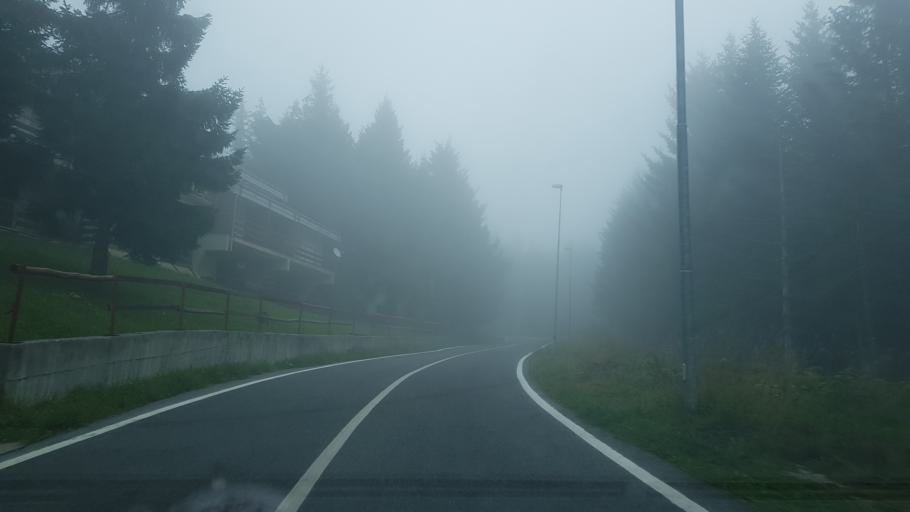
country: IT
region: Piedmont
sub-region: Provincia di Cuneo
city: Frabosa Soprana
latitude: 44.2567
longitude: 7.7921
